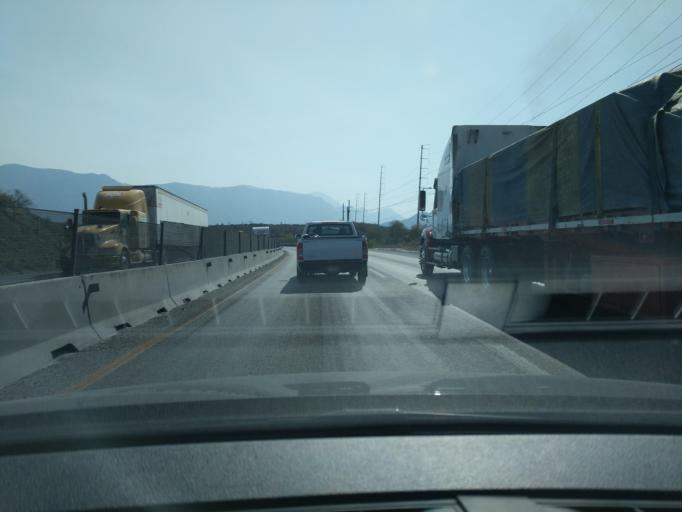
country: MX
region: Nuevo Leon
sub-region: Garcia
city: Los Parques
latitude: 25.7505
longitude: -100.5092
